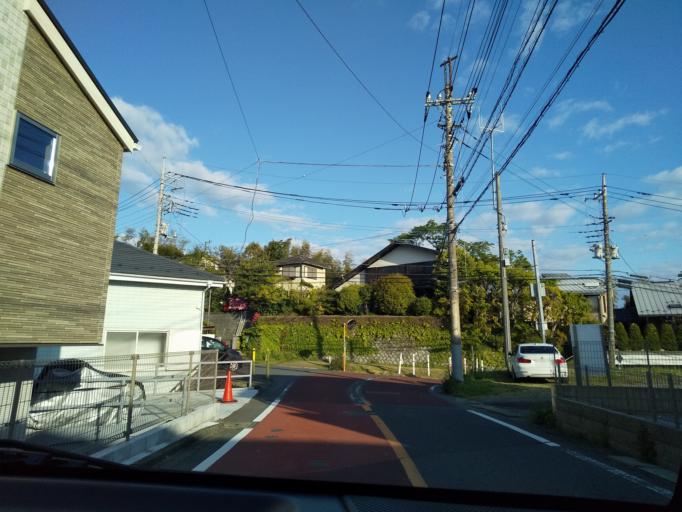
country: JP
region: Tokyo
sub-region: Machida-shi
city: Machida
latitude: 35.5687
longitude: 139.4585
